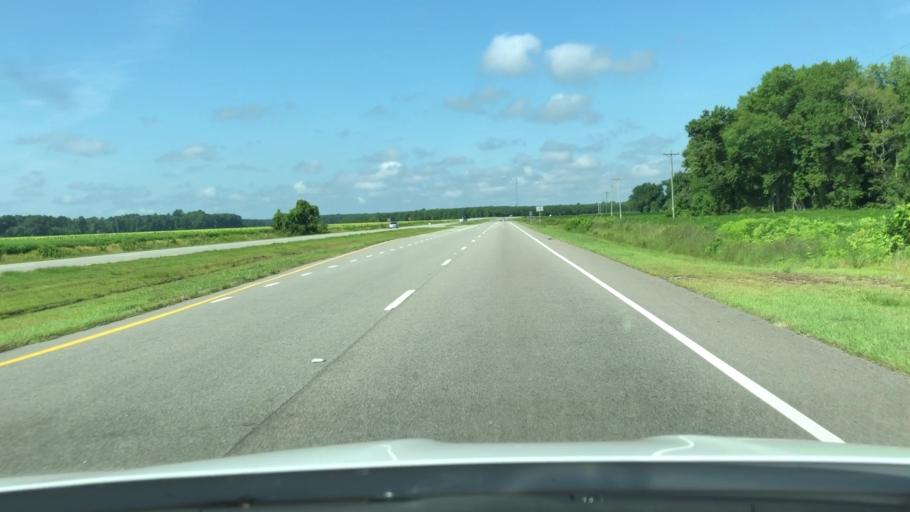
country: US
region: North Carolina
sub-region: Chowan County
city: Edenton
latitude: 36.0387
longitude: -76.7152
